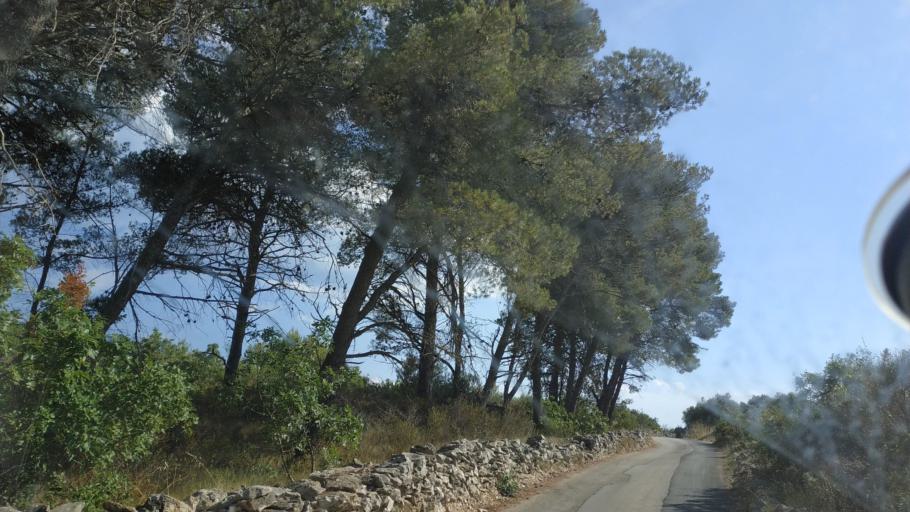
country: HR
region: Splitsko-Dalmatinska
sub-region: Grad Trogir
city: Trogir
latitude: 43.4874
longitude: 16.2477
